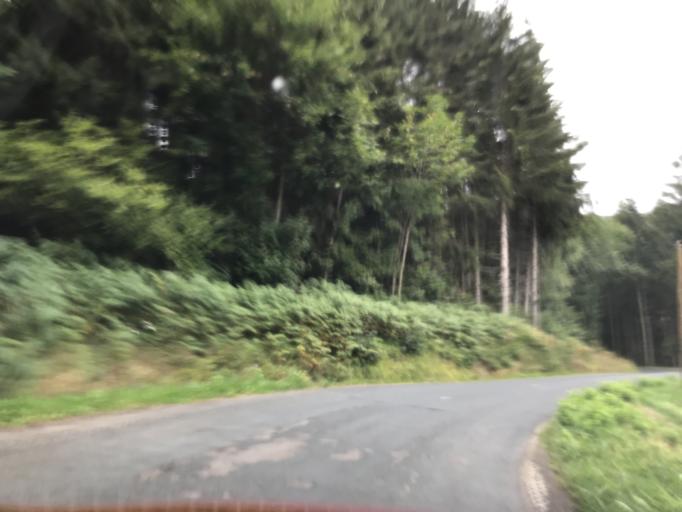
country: FR
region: Rhone-Alpes
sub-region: Departement de la Loire
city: Sail-sous-Couzan
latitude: 45.6839
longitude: 3.9078
